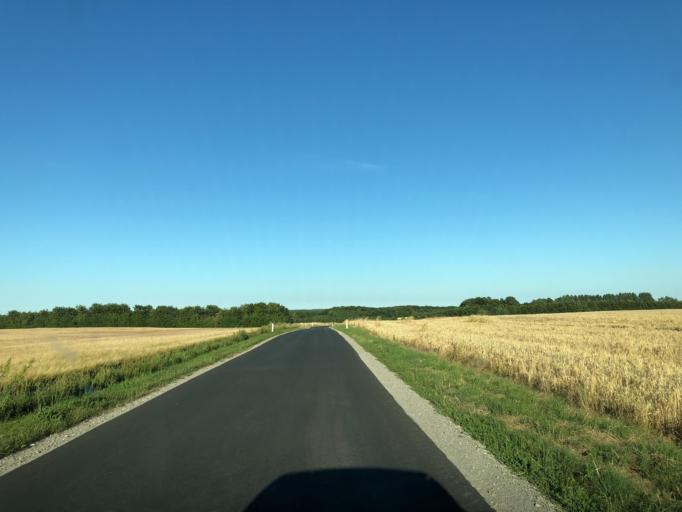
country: DK
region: Central Jutland
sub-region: Horsens Kommune
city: Horsens
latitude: 55.9609
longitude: 9.8298
